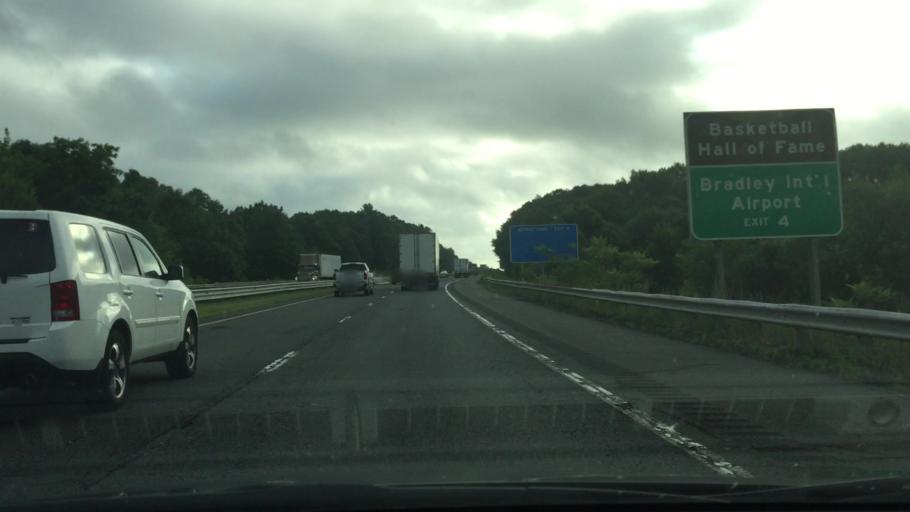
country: US
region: Massachusetts
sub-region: Hampden County
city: Chicopee
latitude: 42.1487
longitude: -72.6708
